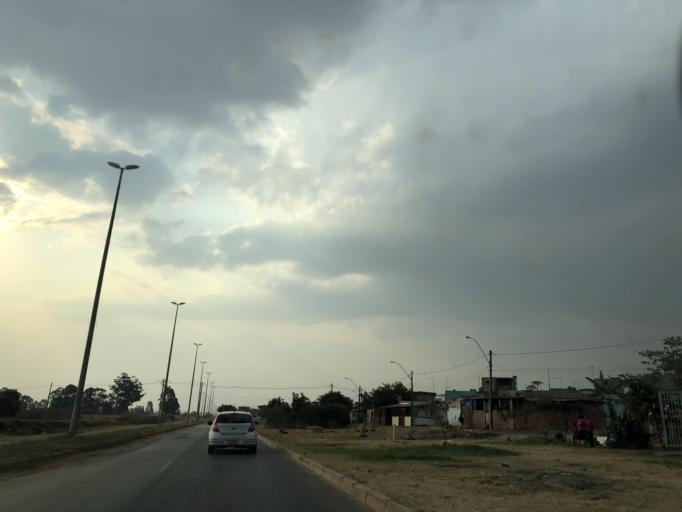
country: BR
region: Federal District
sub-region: Brasilia
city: Brasilia
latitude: -15.9225
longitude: -48.0597
